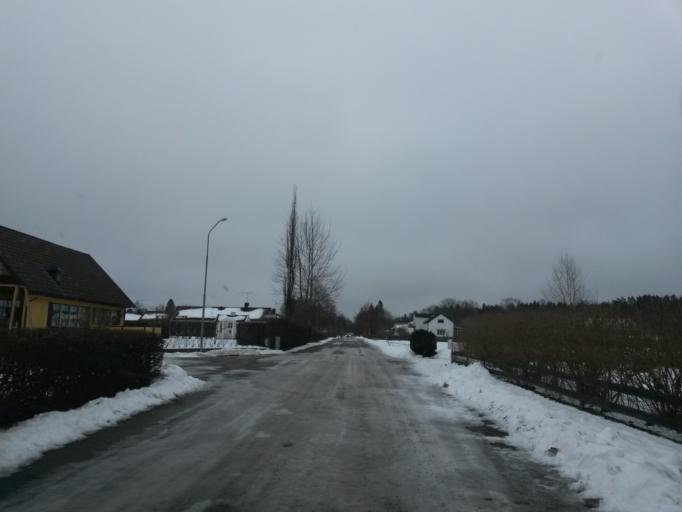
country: SE
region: Vaestra Goetaland
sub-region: Herrljunga Kommun
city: Herrljunga
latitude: 57.9844
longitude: 13.0592
